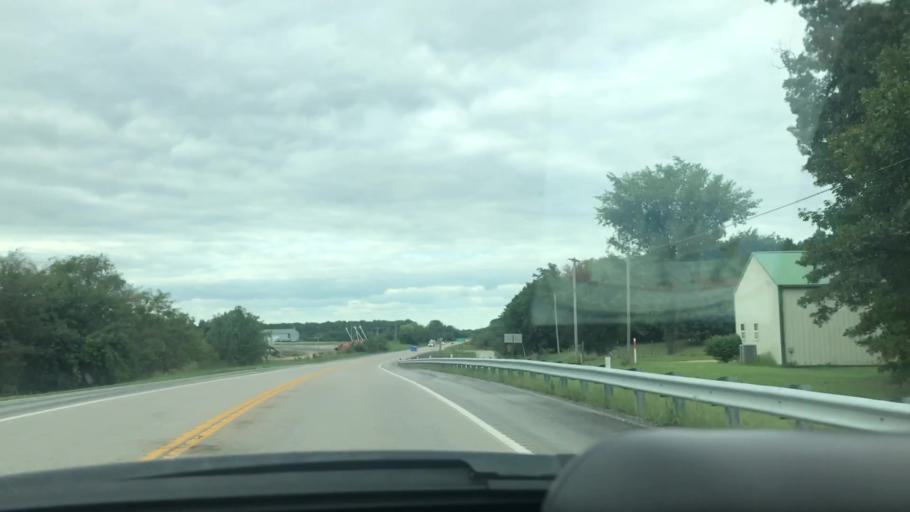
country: US
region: Missouri
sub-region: Benton County
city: Warsaw
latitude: 38.1896
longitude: -93.3235
